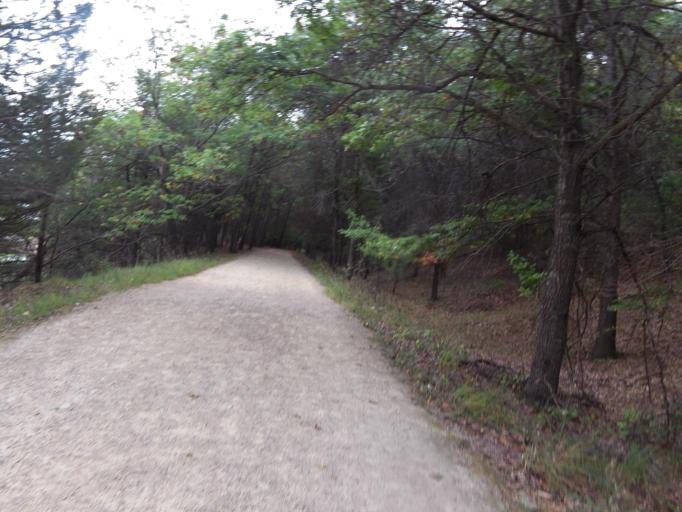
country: US
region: Minnesota
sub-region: Washington County
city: Afton
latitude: 44.8646
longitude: -92.7728
